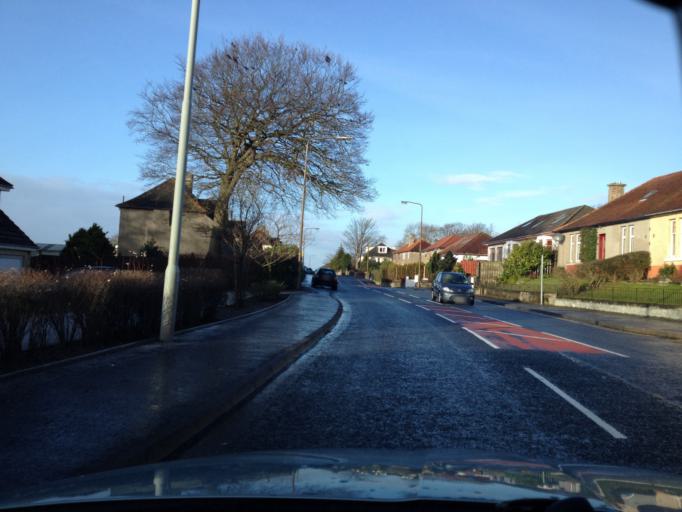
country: GB
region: Scotland
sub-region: West Lothian
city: Bathgate
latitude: 55.8971
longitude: -3.6288
